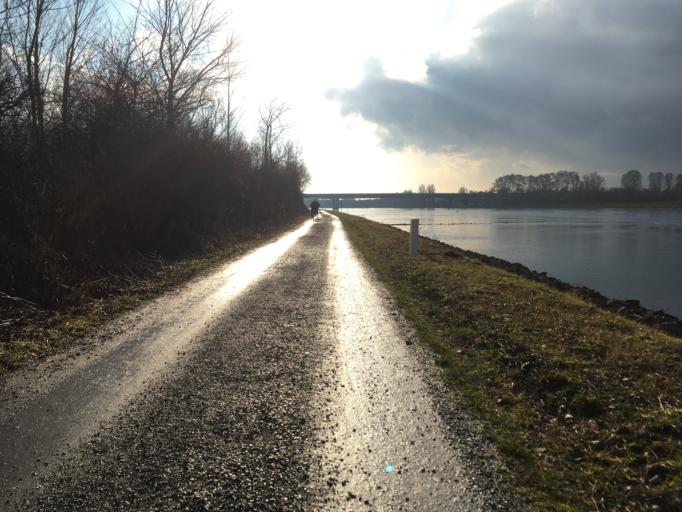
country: DE
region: Rheinland-Pfalz
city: Germersheim
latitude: 49.2337
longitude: 8.3911
